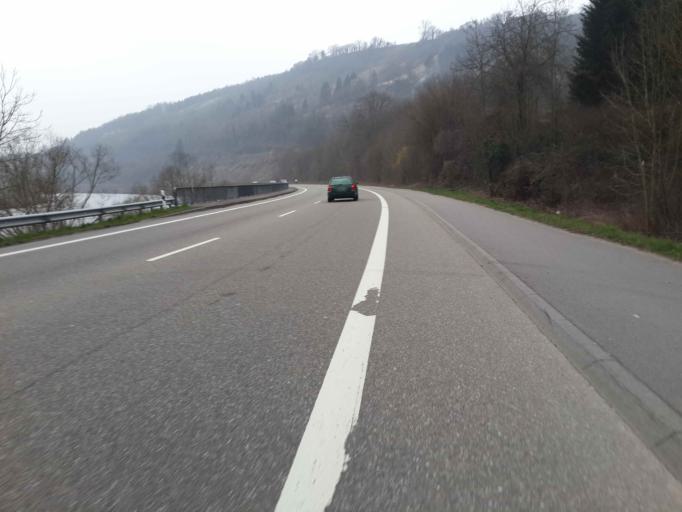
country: DE
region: Baden-Wuerttemberg
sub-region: Karlsruhe Region
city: Obrigheim
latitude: 49.3569
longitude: 9.1047
